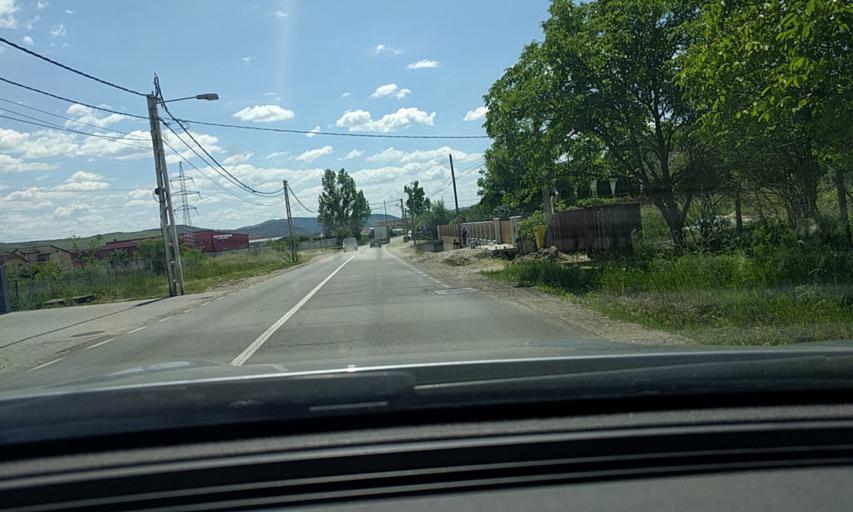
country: RO
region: Bistrita-Nasaud
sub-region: Municipiul Bistrita
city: Viisoara
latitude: 47.1174
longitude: 24.4588
